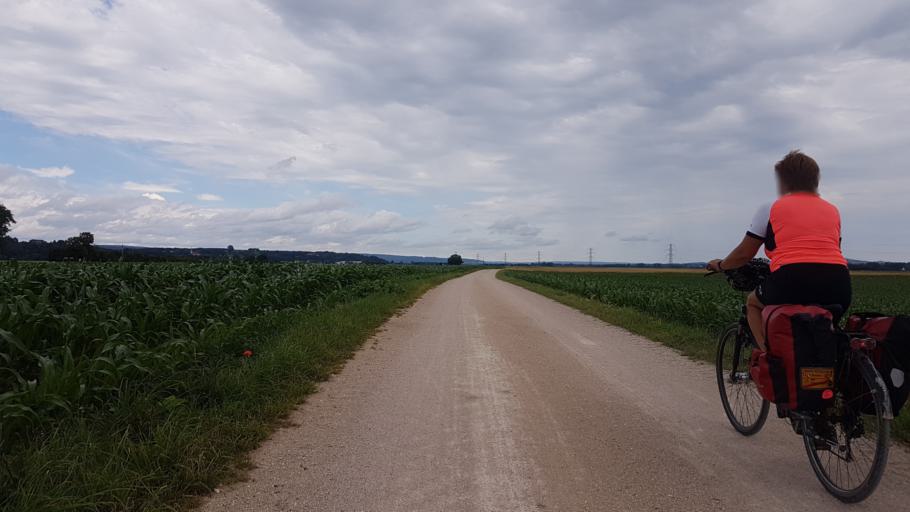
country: DE
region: Baden-Wuerttemberg
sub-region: Tuebingen Region
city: Herbertingen
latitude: 48.0841
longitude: 9.4196
